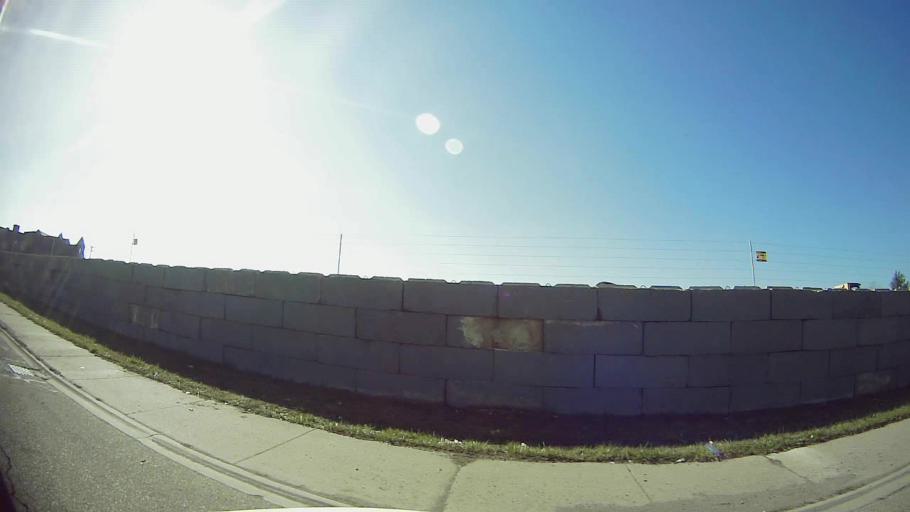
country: US
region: Michigan
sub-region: Wayne County
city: Detroit
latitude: 42.3506
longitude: -83.0875
